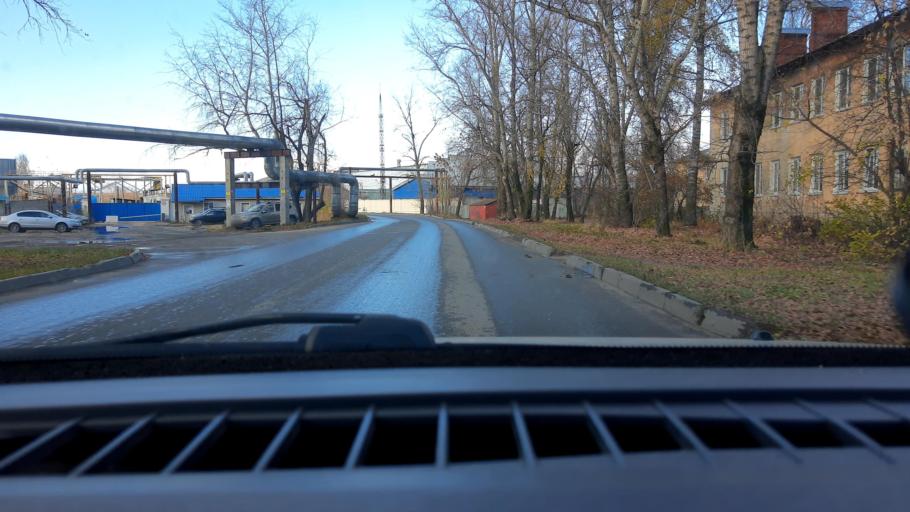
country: RU
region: Nizjnij Novgorod
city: Gorbatovka
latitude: 56.3419
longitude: 43.8239
